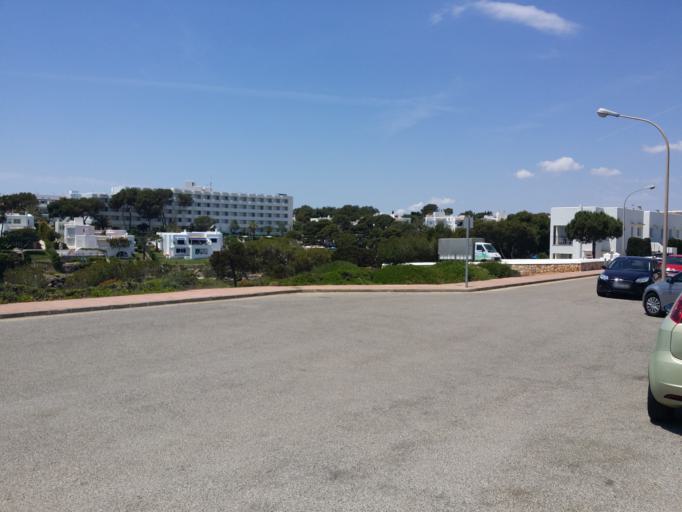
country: ES
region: Balearic Islands
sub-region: Illes Balears
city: Santanyi
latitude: 39.3758
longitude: 3.2396
